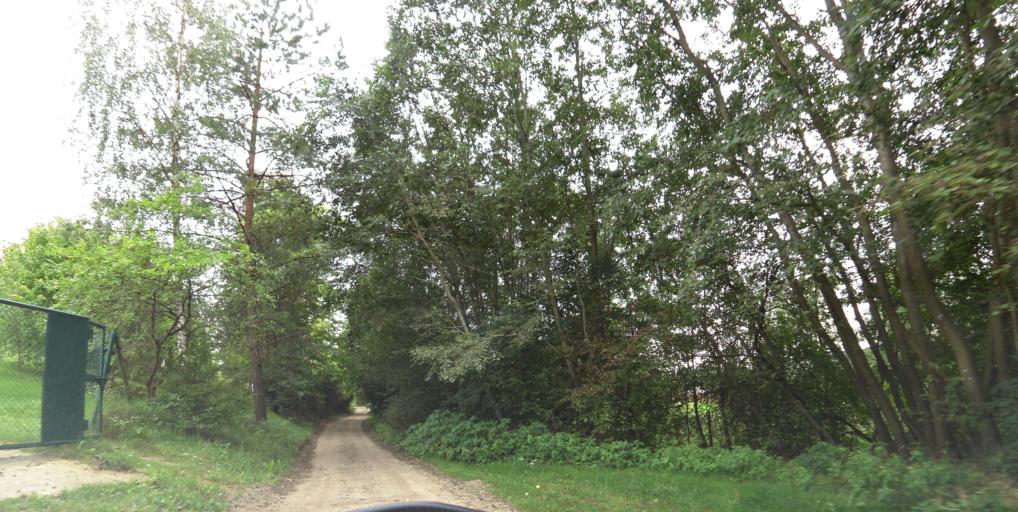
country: LT
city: Grigiskes
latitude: 54.7605
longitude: 25.0210
